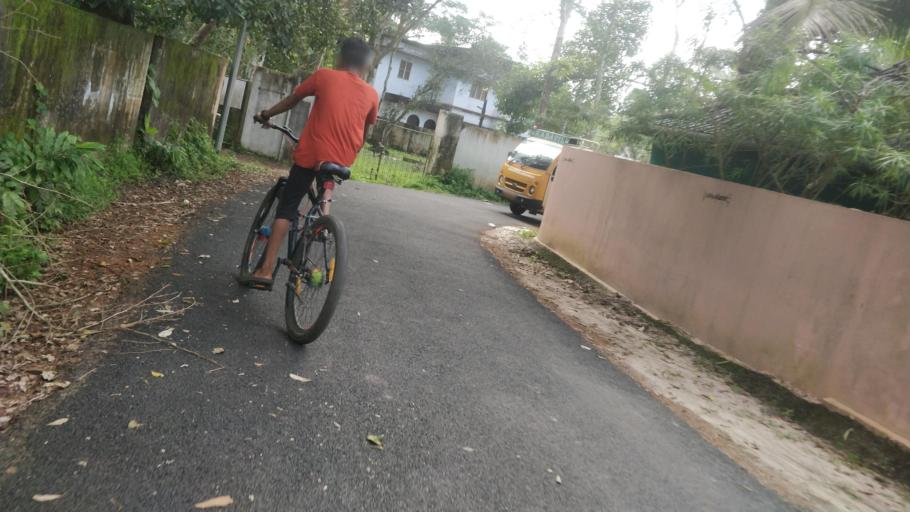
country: IN
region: Kerala
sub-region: Alappuzha
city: Vayalar
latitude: 9.6904
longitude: 76.3309
